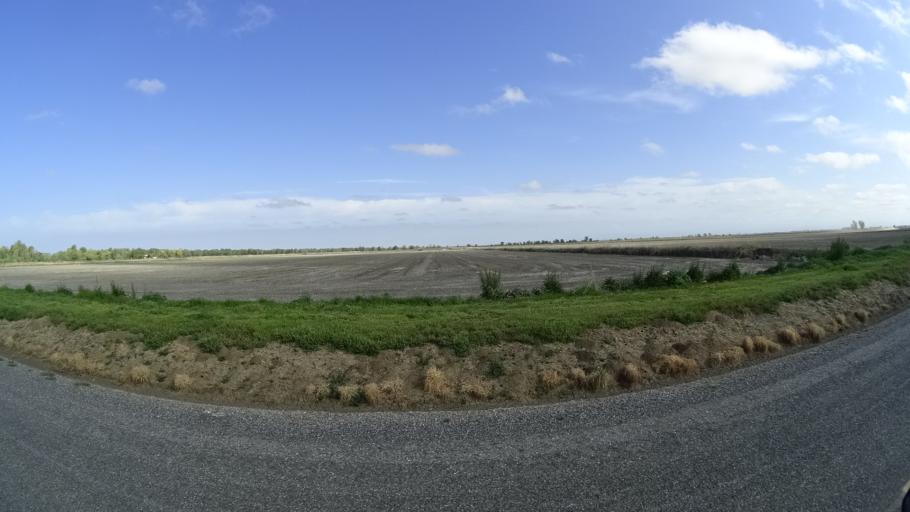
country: US
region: California
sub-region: Butte County
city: Durham
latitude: 39.5222
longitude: -121.9512
